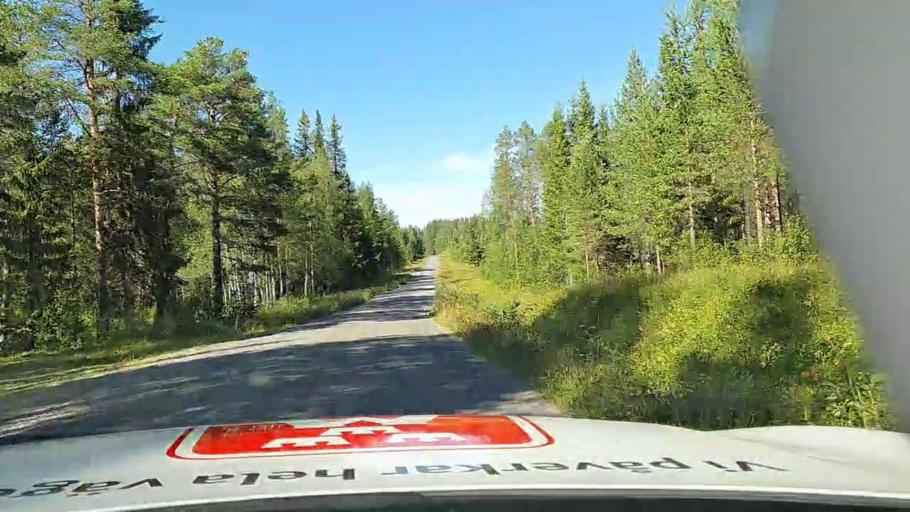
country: SE
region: Jaemtland
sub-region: OEstersunds Kommun
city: Lit
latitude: 63.7686
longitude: 14.6568
